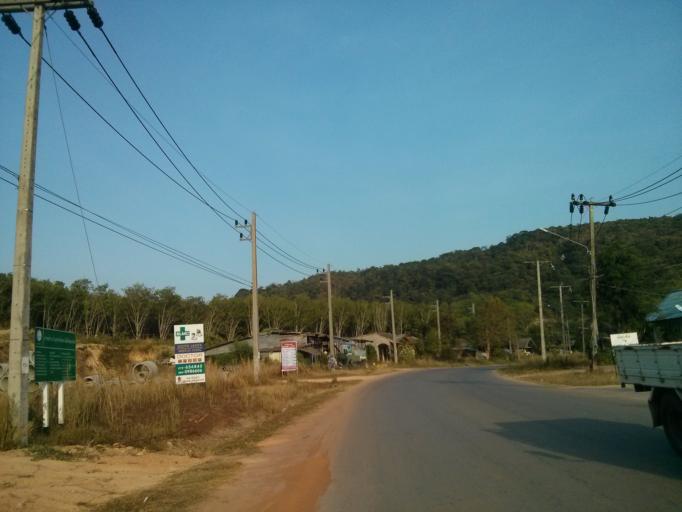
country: TH
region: Krabi
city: Saladan
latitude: 7.5675
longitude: 99.0389
